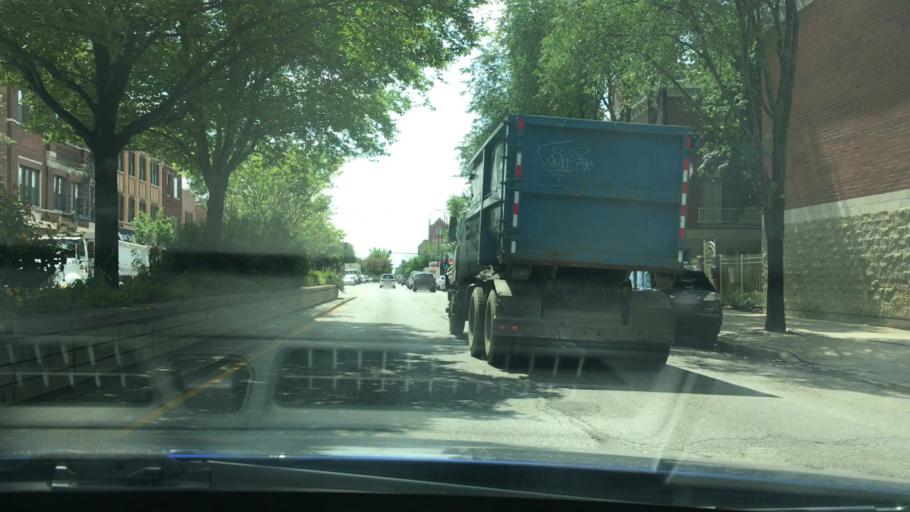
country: US
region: Illinois
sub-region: Cook County
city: Chicago
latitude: 41.8726
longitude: -87.6863
